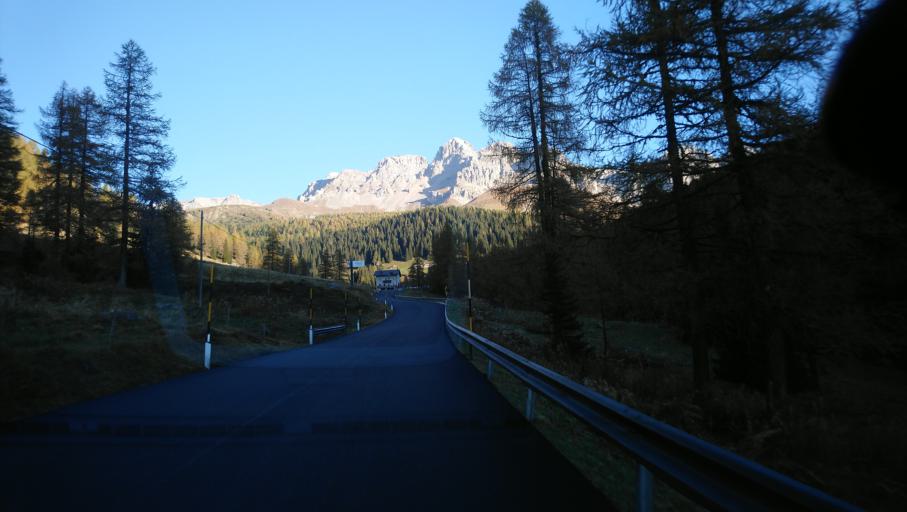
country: IT
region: Veneto
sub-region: Provincia di Belluno
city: Falcade Alto
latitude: 46.3736
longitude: 11.8224
